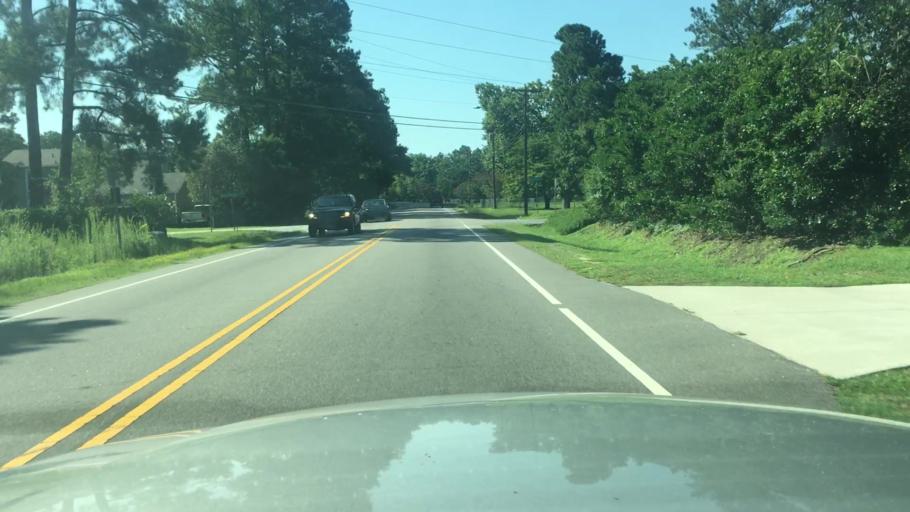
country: US
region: North Carolina
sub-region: Cumberland County
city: Fayetteville
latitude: 35.1077
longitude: -78.9022
